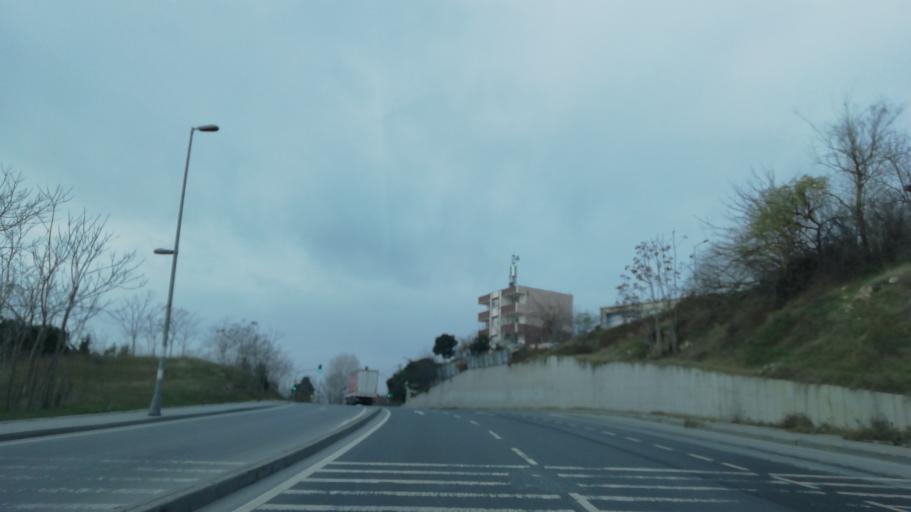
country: TR
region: Istanbul
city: Basaksehir
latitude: 41.0618
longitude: 28.7544
